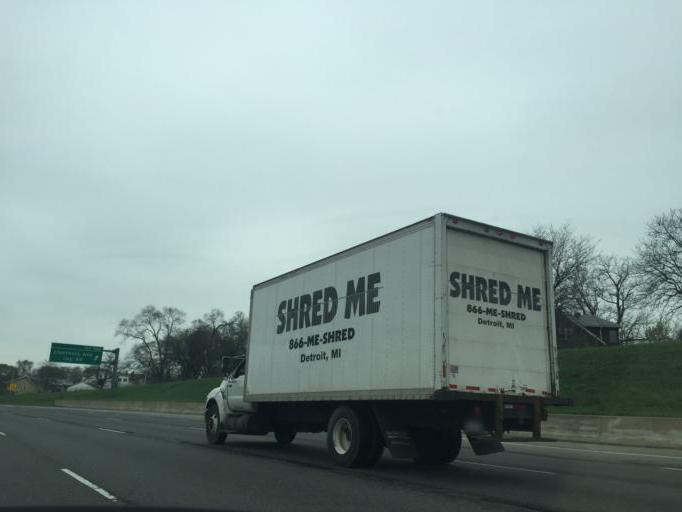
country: US
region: Michigan
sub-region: Wayne County
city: Dearborn
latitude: 42.3704
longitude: -83.1447
